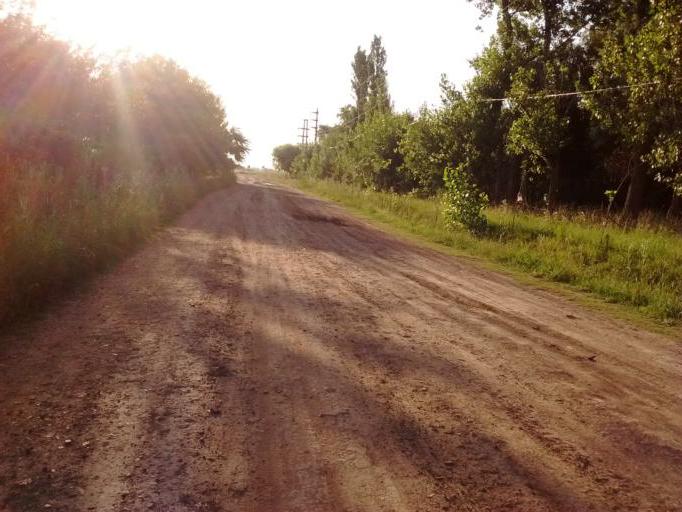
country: AR
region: Santa Fe
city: Roldan
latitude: -32.9309
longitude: -60.8657
